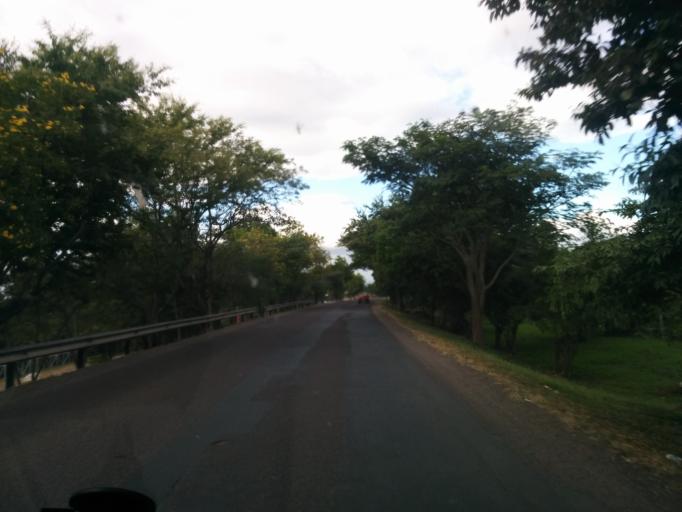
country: NI
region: Esteli
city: Esteli
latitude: 13.1564
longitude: -86.3701
